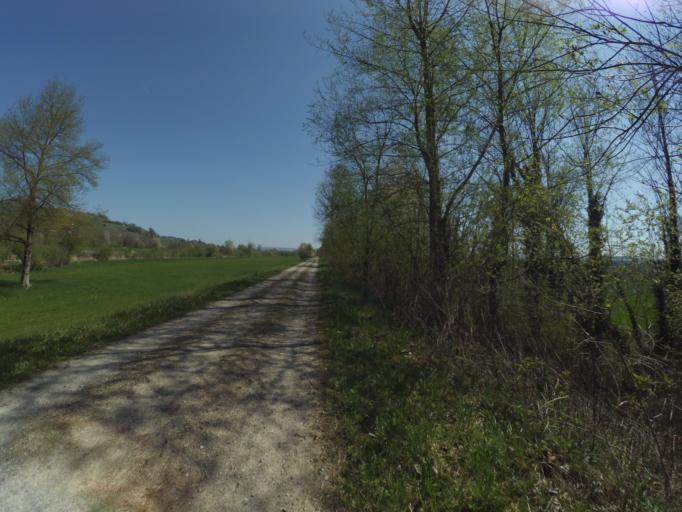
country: CH
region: Zurich
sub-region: Bezirk Winterthur
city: Sulz
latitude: 47.5814
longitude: 8.8105
